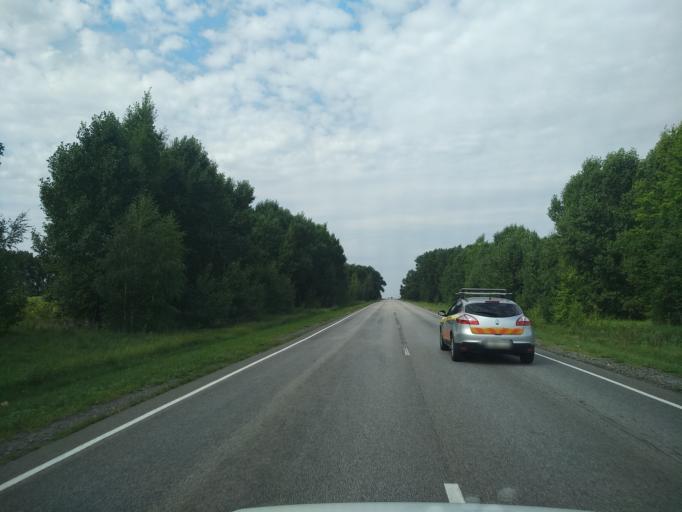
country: RU
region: Voronezj
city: Pereleshinskiy
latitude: 51.8668
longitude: 40.3763
